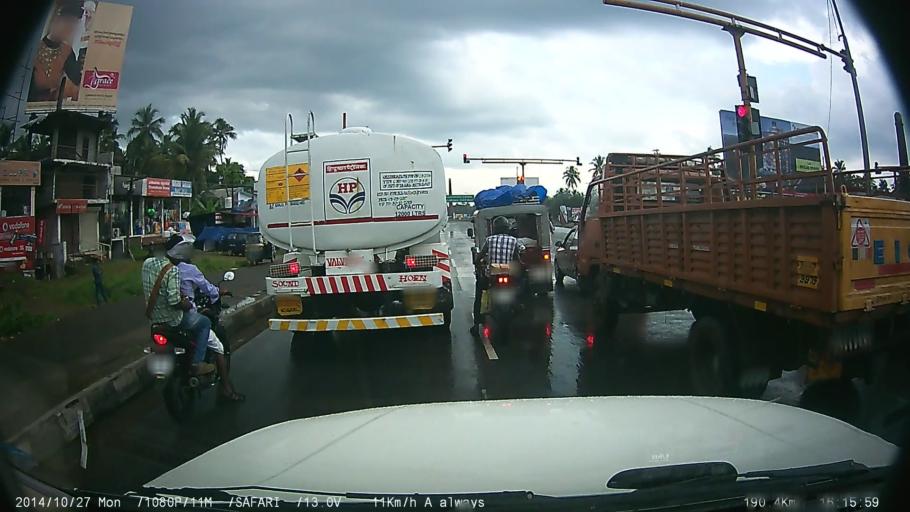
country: IN
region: Kerala
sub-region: Thrissur District
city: Trichur
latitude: 10.4322
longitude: 76.2660
